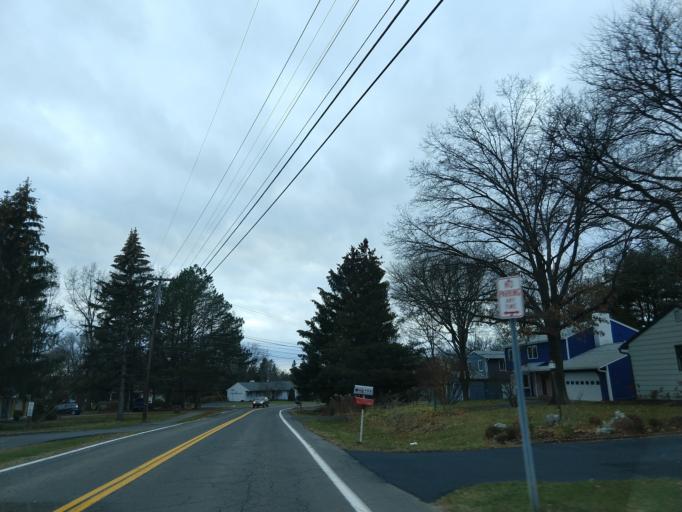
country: US
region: New York
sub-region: Tompkins County
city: Northeast Ithaca
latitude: 42.4740
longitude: -76.4701
